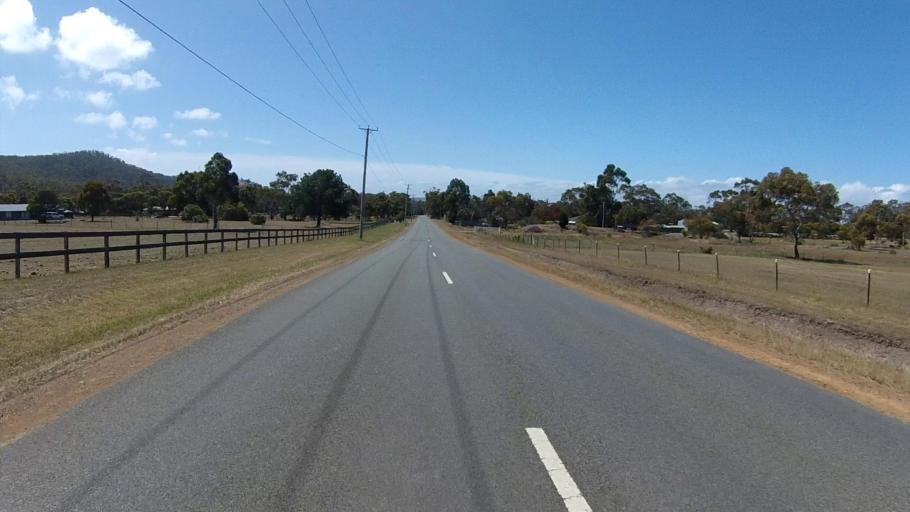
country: AU
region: Tasmania
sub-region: Clarence
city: Sandford
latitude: -42.9514
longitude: 147.4809
